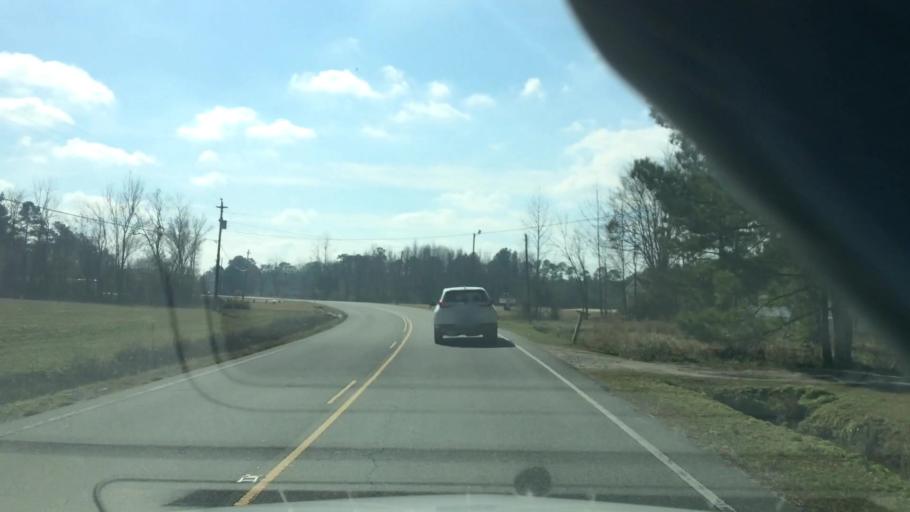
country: US
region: North Carolina
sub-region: Duplin County
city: Beulaville
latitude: 34.8822
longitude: -77.7886
